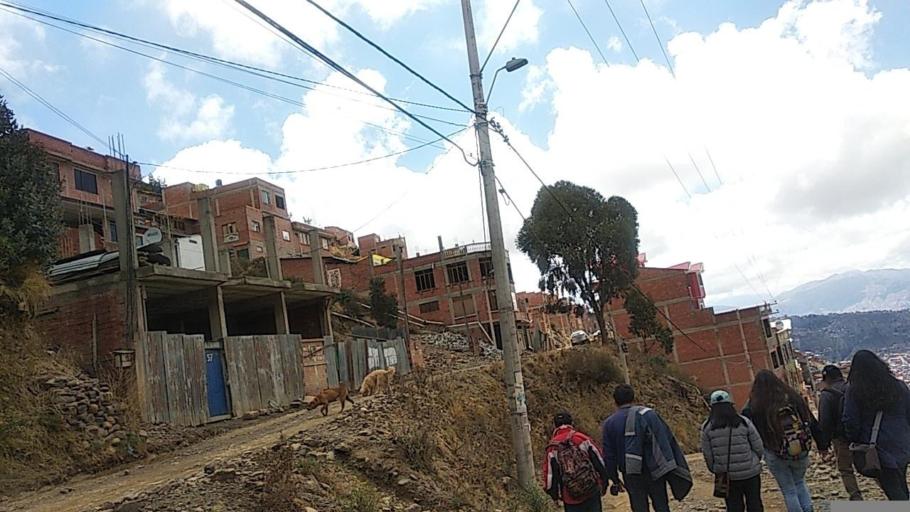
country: BO
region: La Paz
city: La Paz
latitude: -16.4667
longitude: -68.1336
